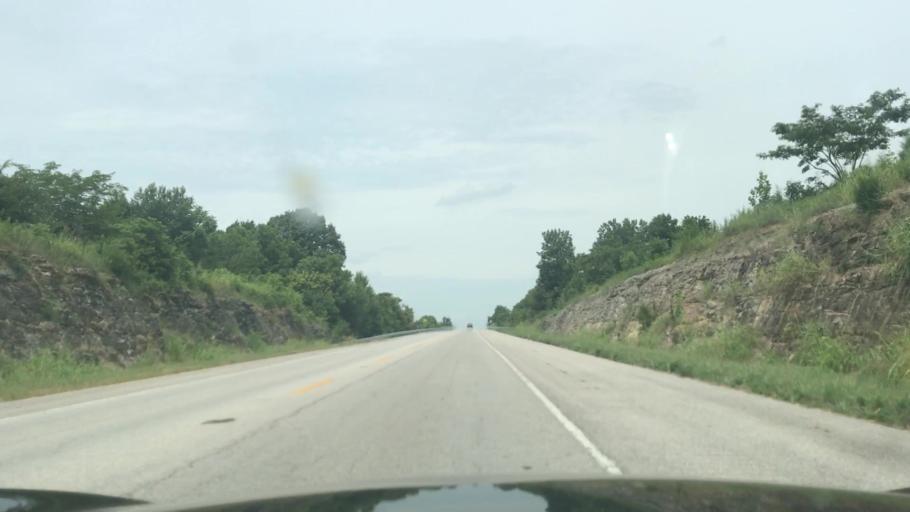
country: US
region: Kentucky
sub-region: Green County
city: Greensburg
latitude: 37.2790
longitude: -85.5130
